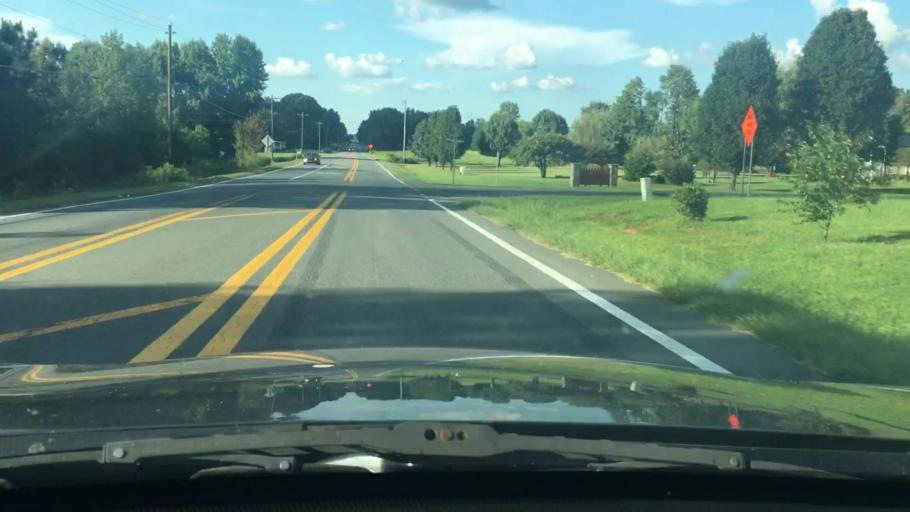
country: US
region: North Carolina
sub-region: Alamance County
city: Green Level
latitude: 36.1996
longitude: -79.3227
